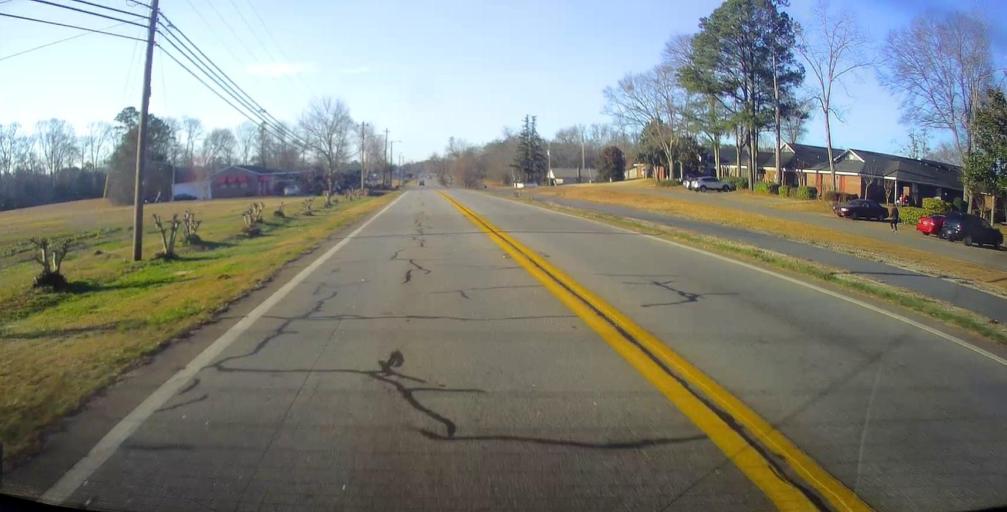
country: US
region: Georgia
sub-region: Harris County
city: Pine Mountain
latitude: 32.8576
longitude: -84.8499
